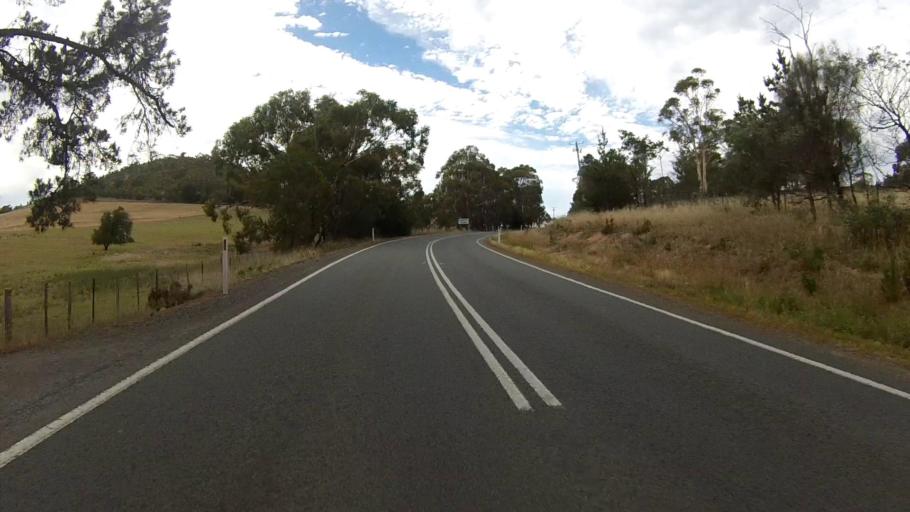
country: AU
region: Tasmania
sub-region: Sorell
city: Sorell
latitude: -42.7029
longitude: 147.4937
